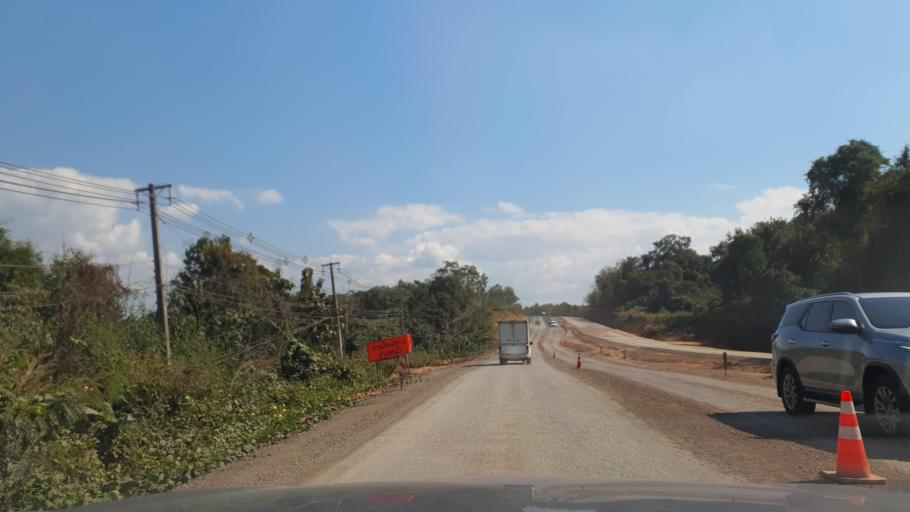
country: TH
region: Nan
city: Nan
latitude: 18.8282
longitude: 100.7603
